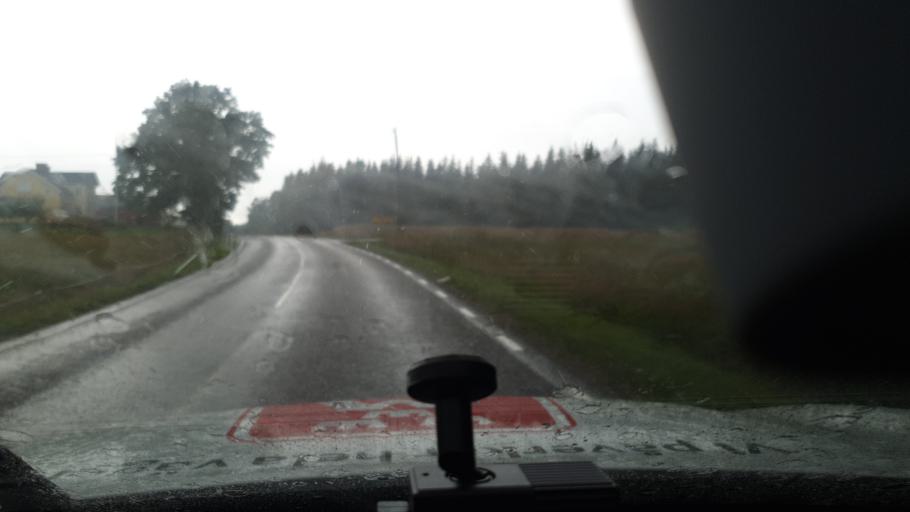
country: SE
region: Vaermland
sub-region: Sunne Kommun
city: Sunne
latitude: 59.7918
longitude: 13.0787
